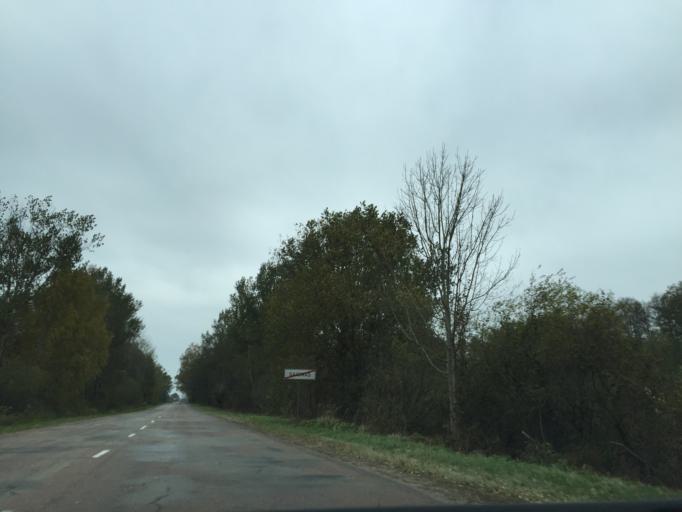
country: LV
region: Marupe
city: Marupe
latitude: 56.8529
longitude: 24.0541
